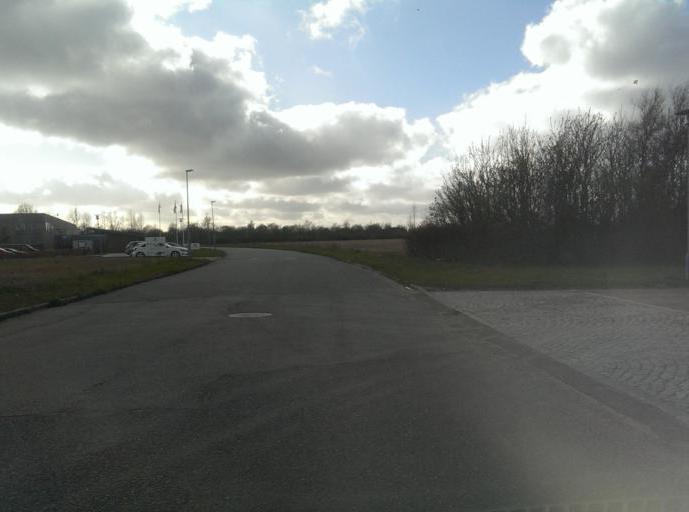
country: DK
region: South Denmark
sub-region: Esbjerg Kommune
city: Esbjerg
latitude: 55.5168
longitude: 8.4623
